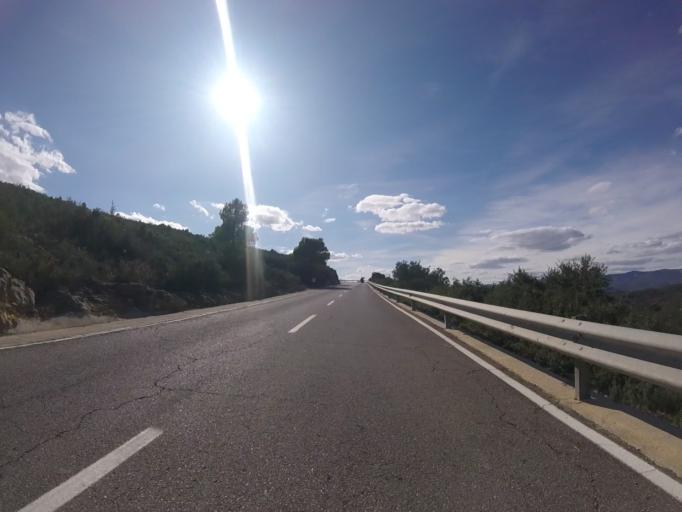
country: ES
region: Valencia
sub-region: Provincia de Castello
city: Cuevas de Vinroma
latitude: 40.2960
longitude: 0.1741
